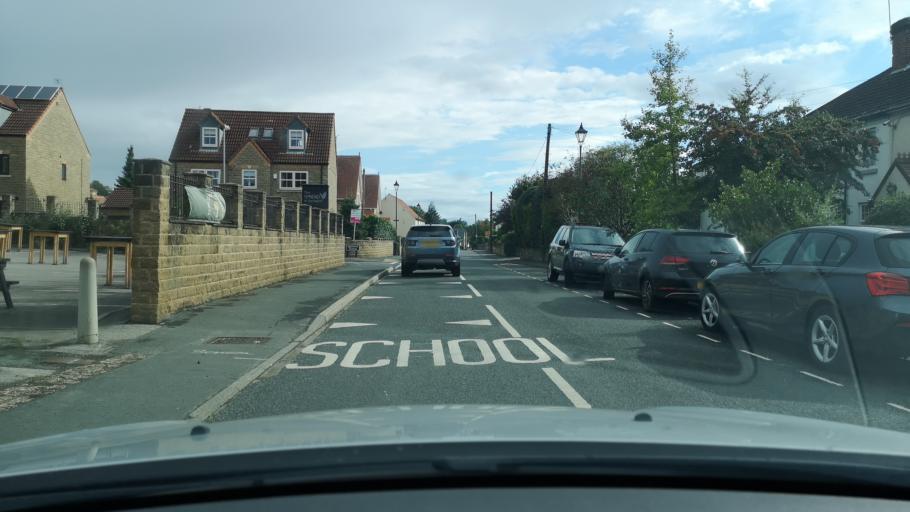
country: GB
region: England
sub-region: City and Borough of Wakefield
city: Darrington
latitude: 53.6749
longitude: -1.2704
